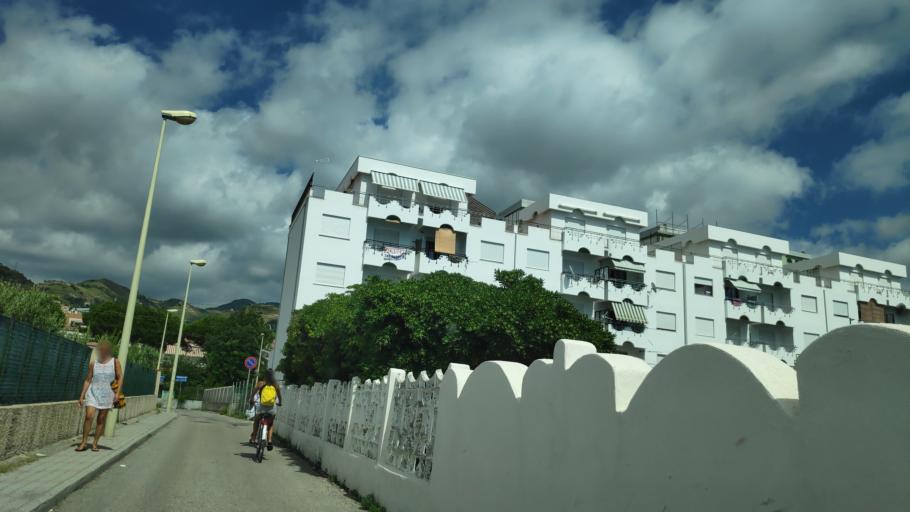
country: IT
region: Calabria
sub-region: Provincia di Cosenza
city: Amantea
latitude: 39.1257
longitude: 16.0708
